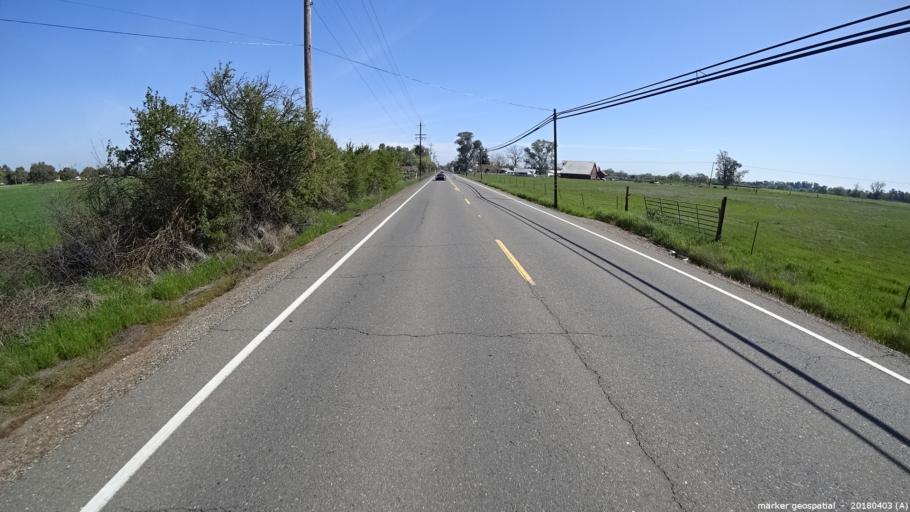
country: US
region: California
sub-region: Sacramento County
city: Wilton
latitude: 38.3981
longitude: -121.2625
